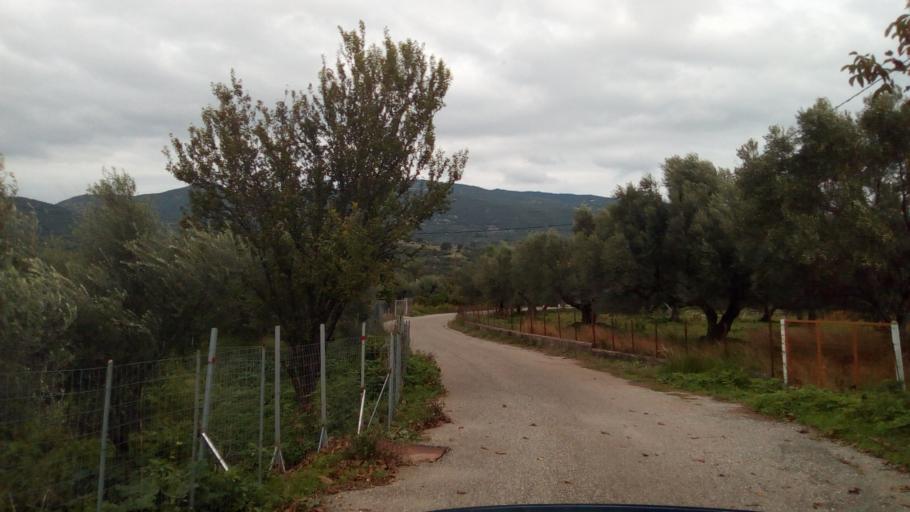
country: GR
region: West Greece
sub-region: Nomos Achaias
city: Kamarai
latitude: 38.4152
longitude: 21.9528
